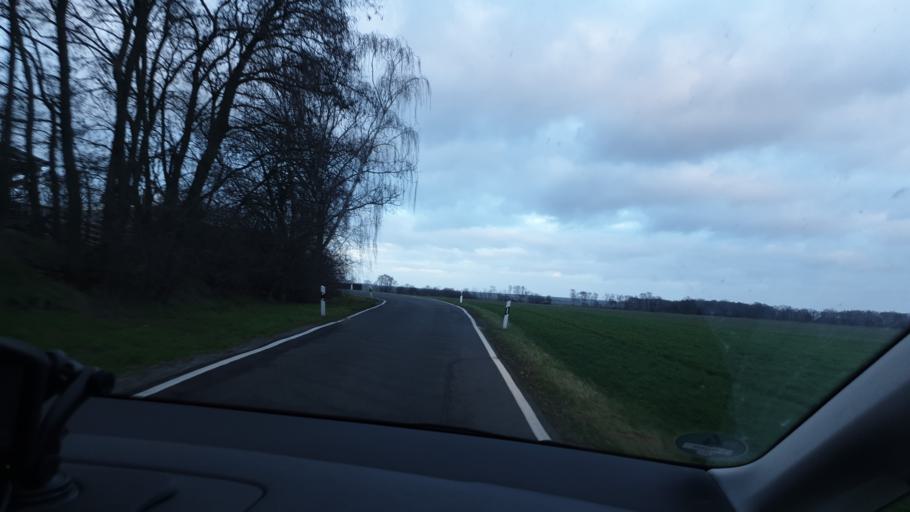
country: DE
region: Saxony
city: Mockrehna
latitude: 51.4649
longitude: 12.8572
